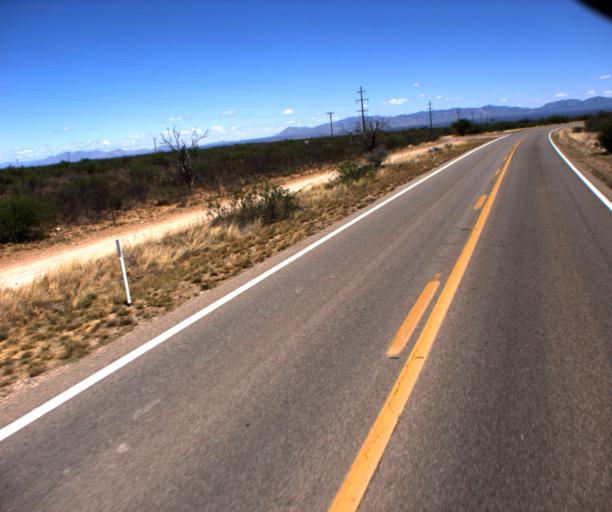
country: US
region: Arizona
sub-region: Cochise County
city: Huachuca City
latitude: 31.7072
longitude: -110.2836
